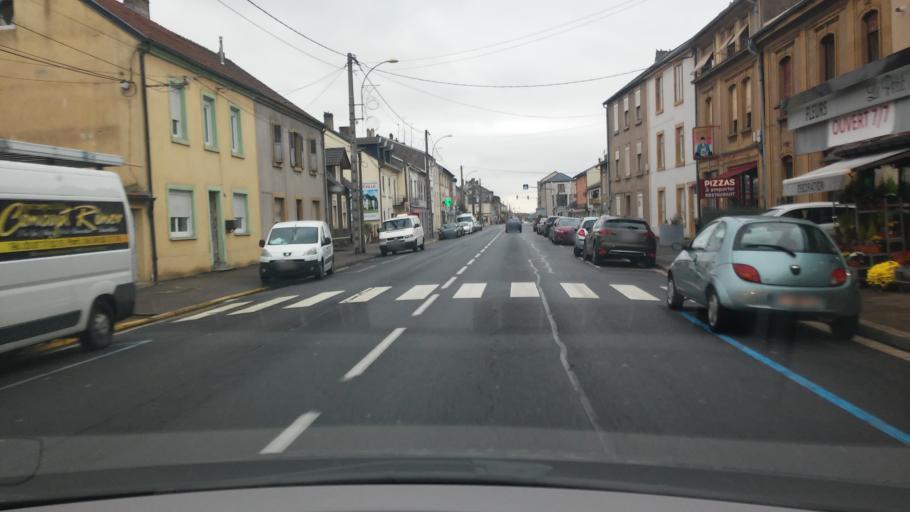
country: FR
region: Lorraine
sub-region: Departement de la Moselle
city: Mondelange
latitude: 49.2596
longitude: 6.1699
